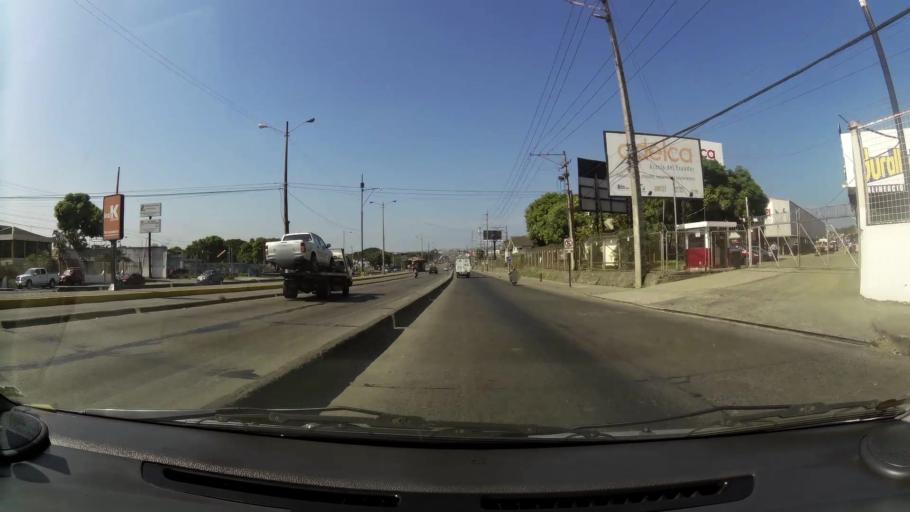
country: EC
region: Guayas
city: Santa Lucia
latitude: -2.1112
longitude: -79.9337
